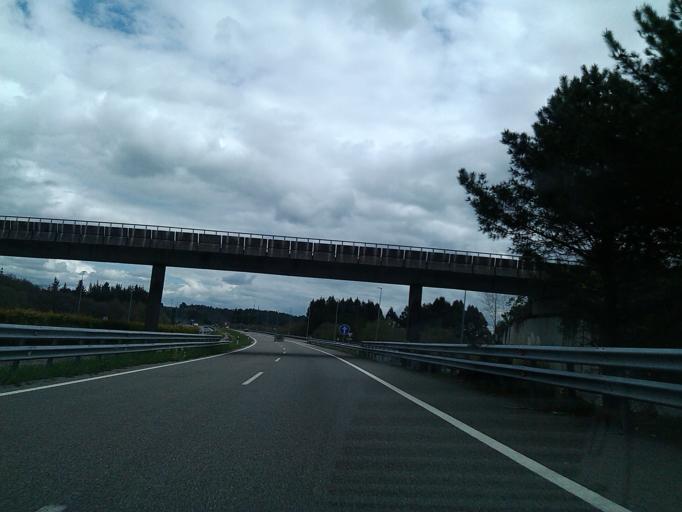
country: ES
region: Galicia
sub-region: Provincia de Lugo
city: Guitiriz
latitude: 43.1877
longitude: -7.9259
